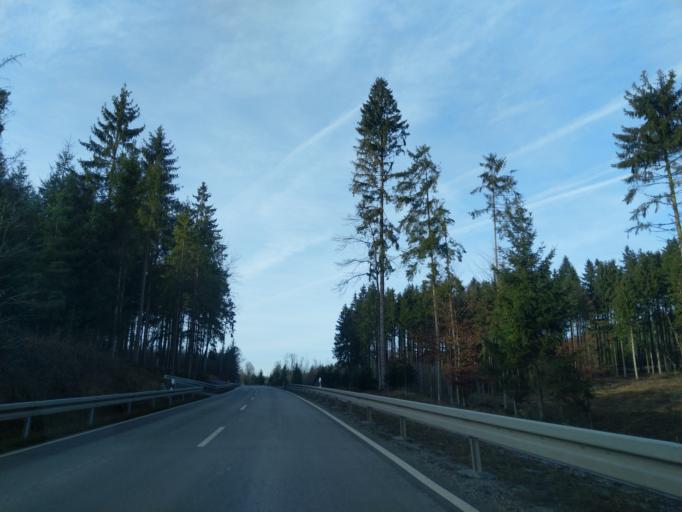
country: DE
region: Bavaria
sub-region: Lower Bavaria
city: Wallerfing
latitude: 48.6623
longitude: 12.8748
